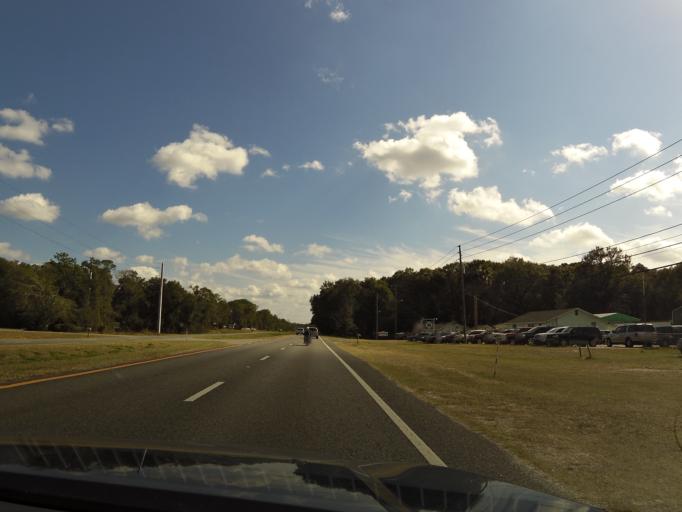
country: US
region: Florida
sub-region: Volusia County
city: North DeLand
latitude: 29.0772
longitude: -81.3128
